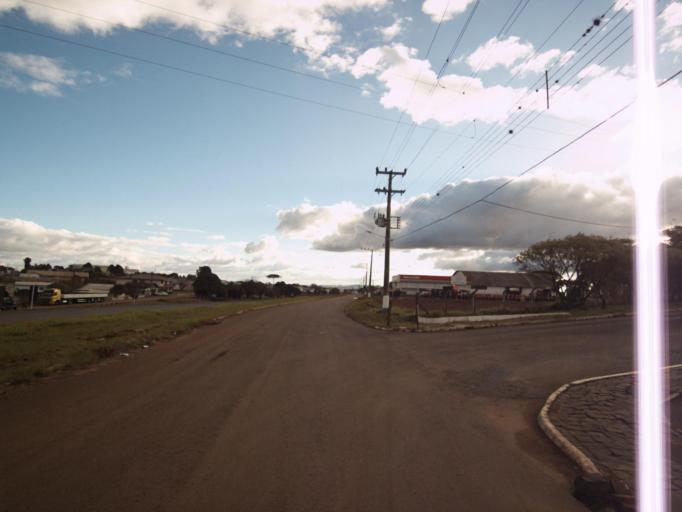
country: BR
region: Santa Catarina
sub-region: Campos Novos
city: Campos Novos
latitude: -27.3905
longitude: -51.2172
